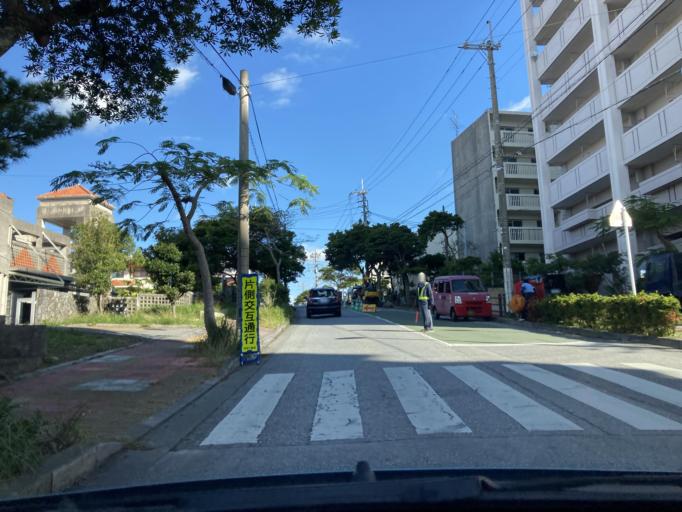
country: JP
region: Okinawa
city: Ginowan
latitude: 26.2258
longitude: 127.7324
